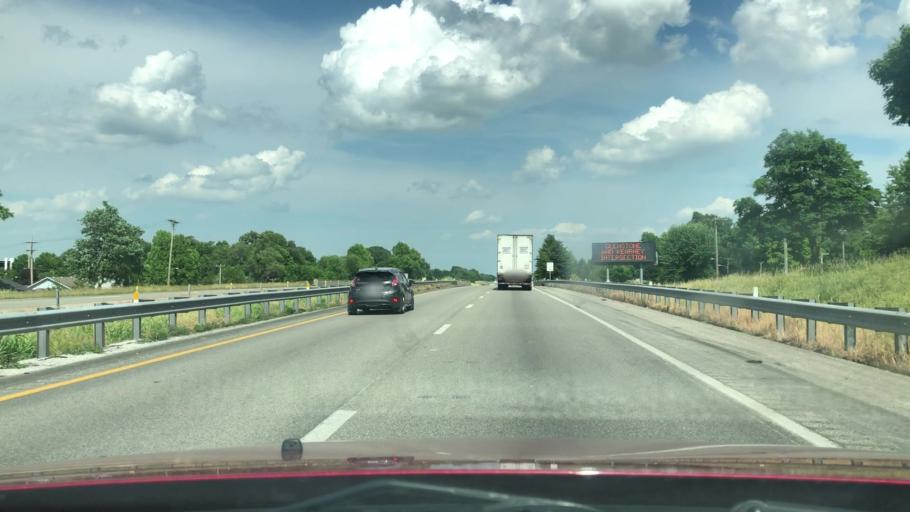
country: US
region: Missouri
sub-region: Greene County
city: Springfield
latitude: 37.2502
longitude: -93.2988
